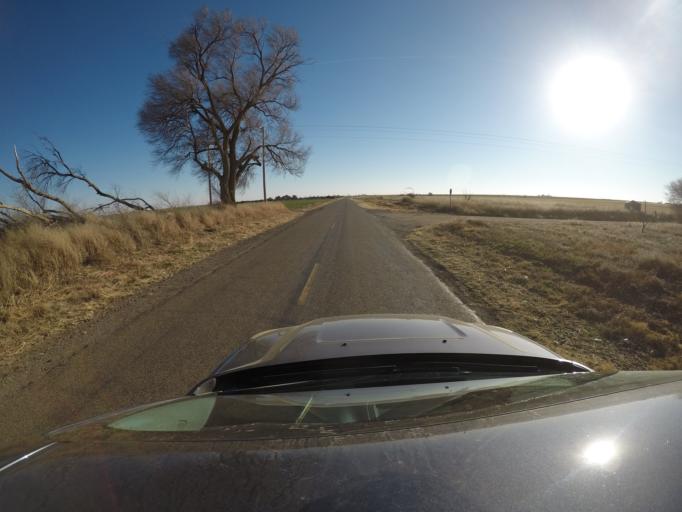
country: US
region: Texas
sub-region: Parmer County
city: Farwell
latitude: 34.3175
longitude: -103.0438
